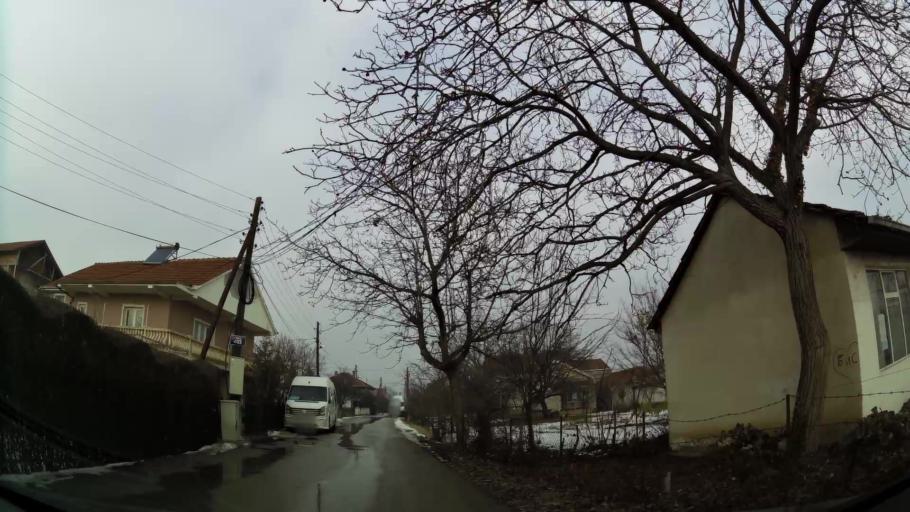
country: MK
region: Ilinden
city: Marino
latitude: 41.9950
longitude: 21.5868
